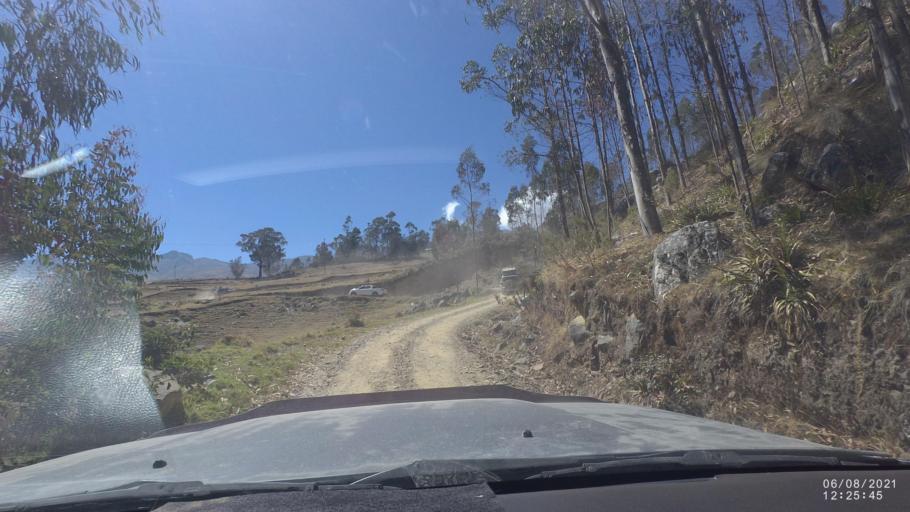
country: BO
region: Cochabamba
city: Colchani
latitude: -16.7939
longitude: -66.6561
